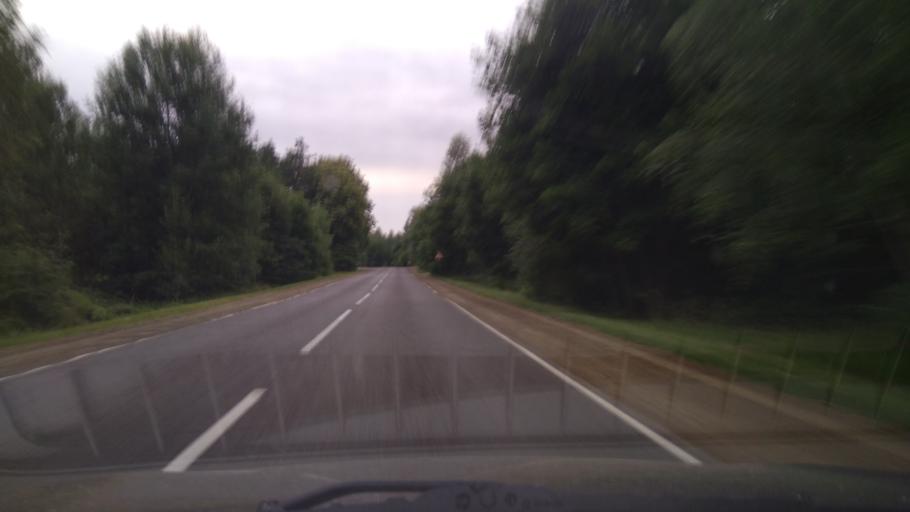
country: BY
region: Brest
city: Byaroza
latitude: 52.4112
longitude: 24.9928
